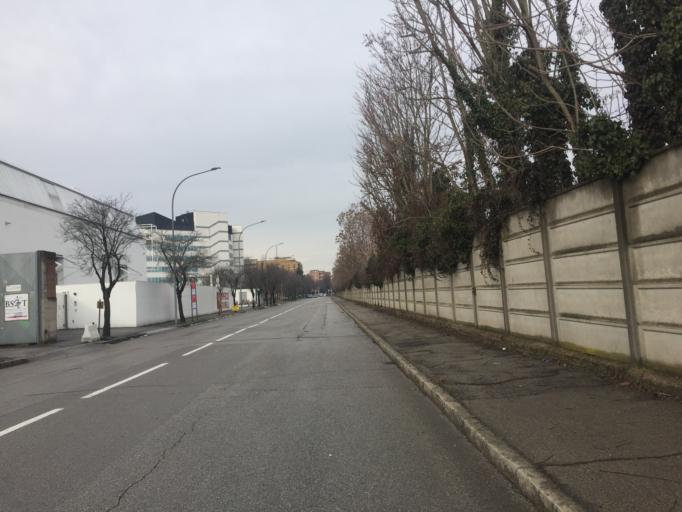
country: IT
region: Emilia-Romagna
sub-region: Provincia di Bologna
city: Bologna
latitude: 44.5087
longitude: 11.3080
